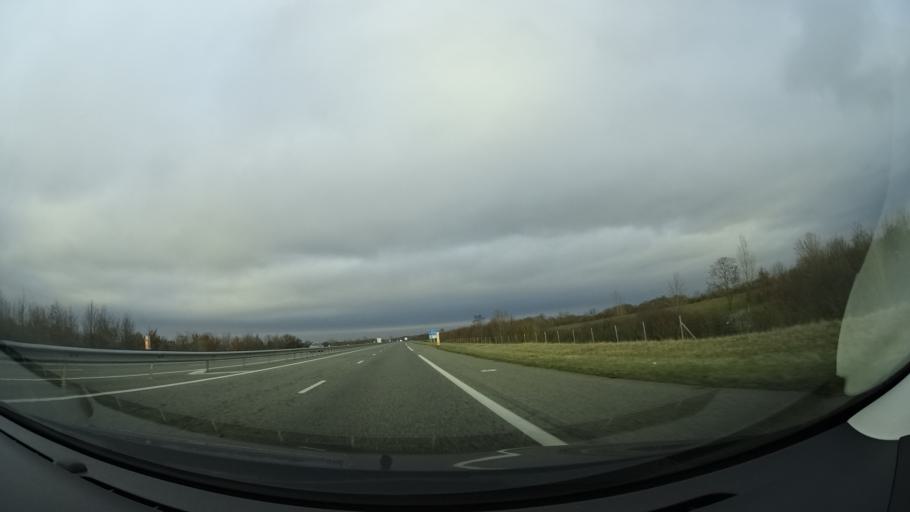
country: FR
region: Midi-Pyrenees
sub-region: Departement de l'Ariege
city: Pamiers
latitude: 43.1663
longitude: 1.6182
